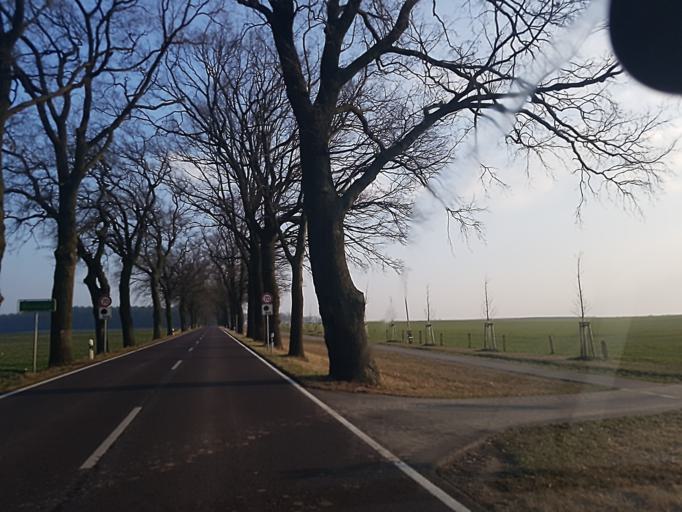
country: DE
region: Brandenburg
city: Gorzke
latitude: 52.1588
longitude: 12.3876
